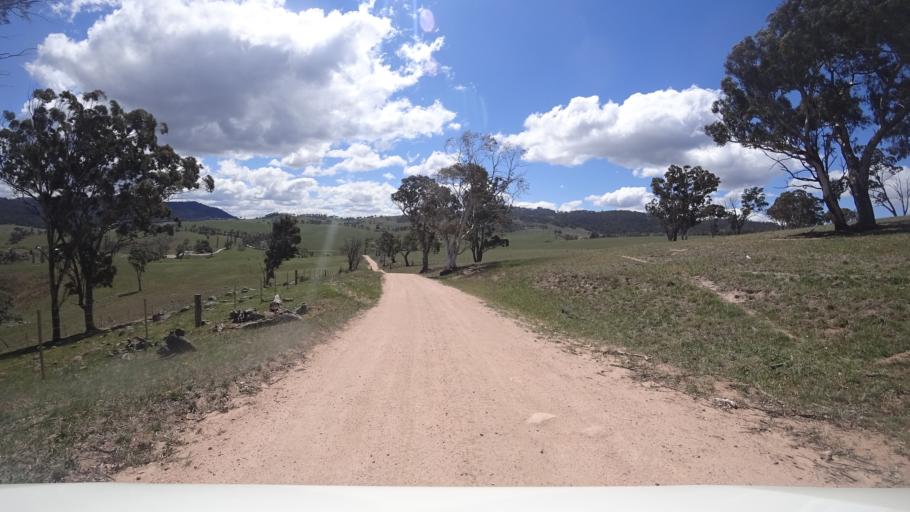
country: AU
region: New South Wales
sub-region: Oberon
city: Oberon
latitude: -33.5714
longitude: 149.9419
